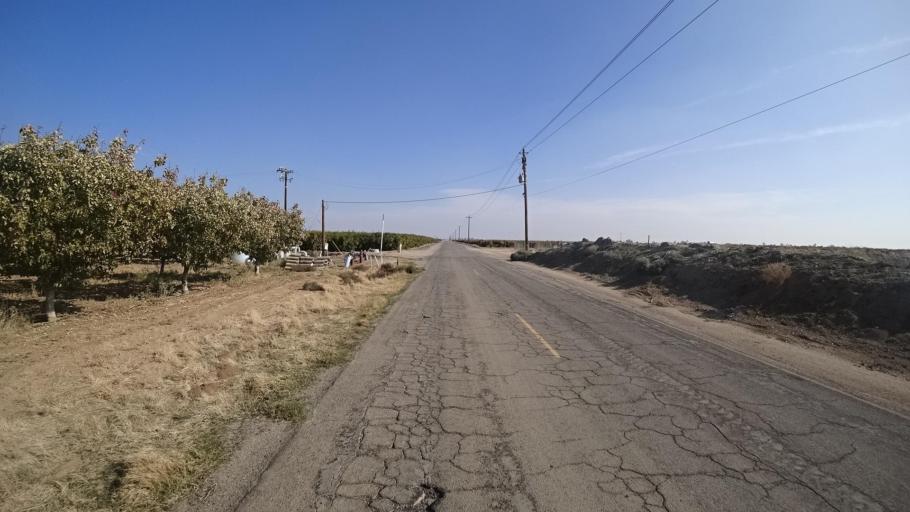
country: US
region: California
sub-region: Kern County
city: Greenacres
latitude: 35.5299
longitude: -119.1253
